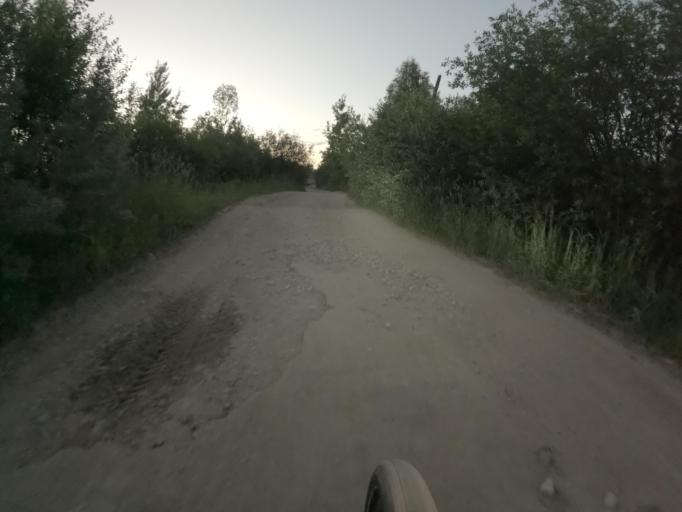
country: RU
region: St.-Petersburg
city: Sapernyy
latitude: 59.7812
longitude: 30.6733
